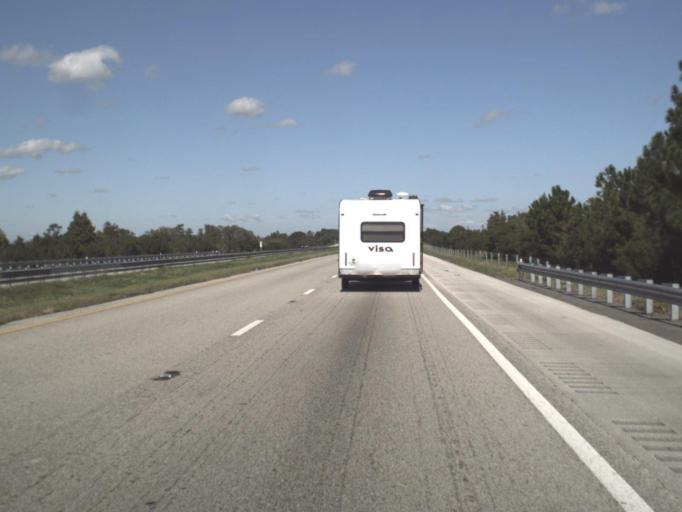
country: US
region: Florida
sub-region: Brevard County
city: June Park
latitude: 27.9050
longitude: -81.0468
